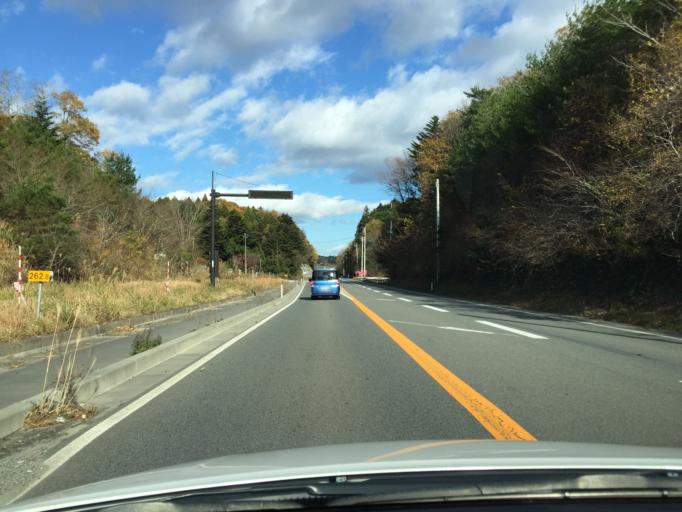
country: JP
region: Fukushima
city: Namie
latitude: 37.5110
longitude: 140.9981
